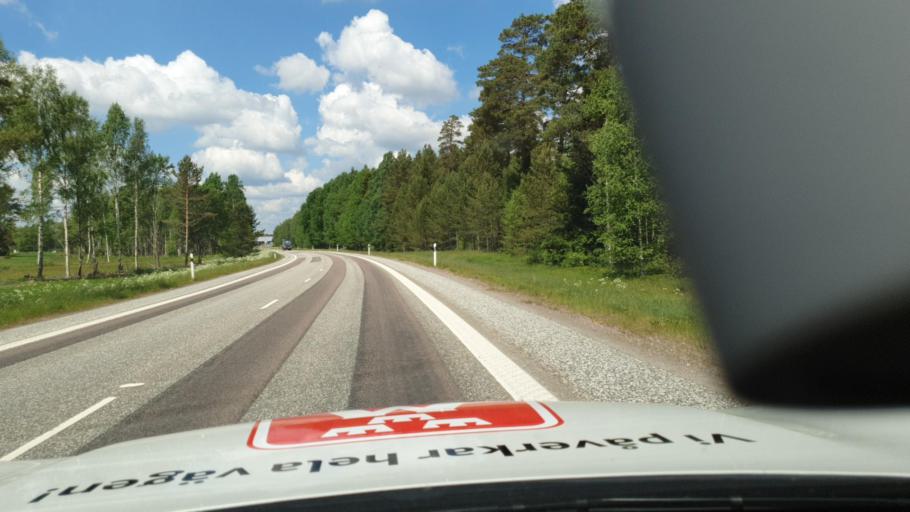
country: SE
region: Joenkoeping
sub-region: Jonkopings Kommun
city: Odensjo
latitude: 57.6407
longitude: 14.2035
